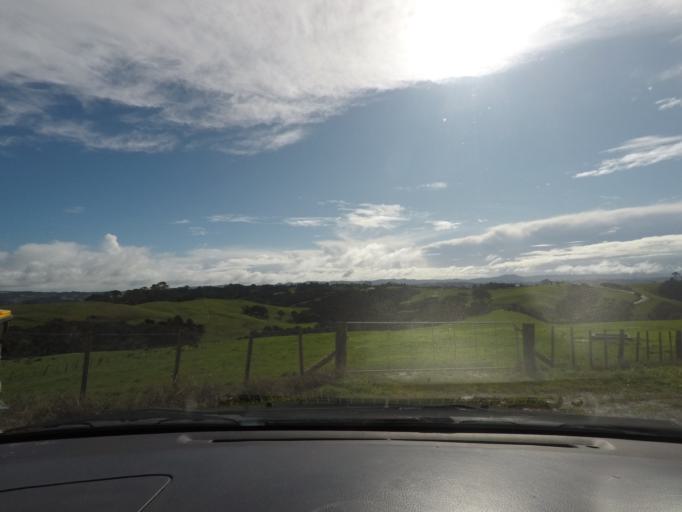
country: NZ
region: Auckland
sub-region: Auckland
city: Warkworth
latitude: -36.4540
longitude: 174.7505
